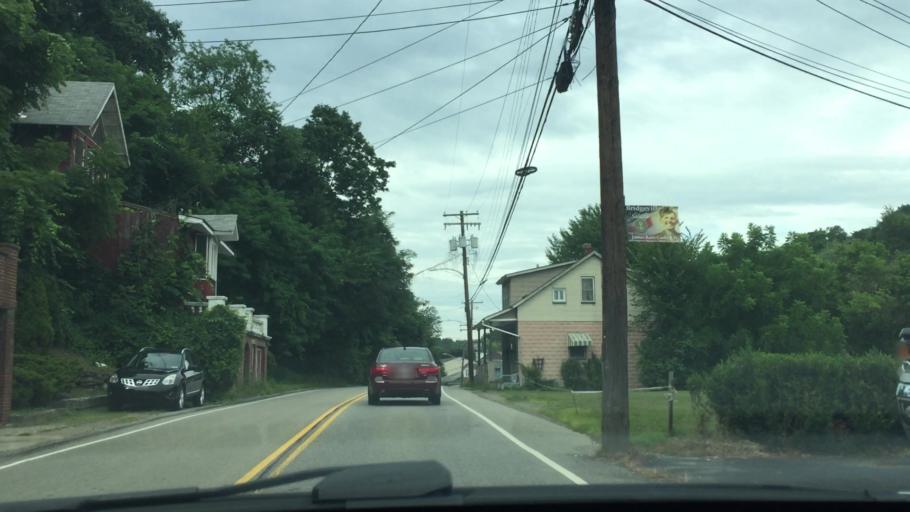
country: US
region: Pennsylvania
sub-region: Allegheny County
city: Bridgeville
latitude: 40.3591
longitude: -80.1031
